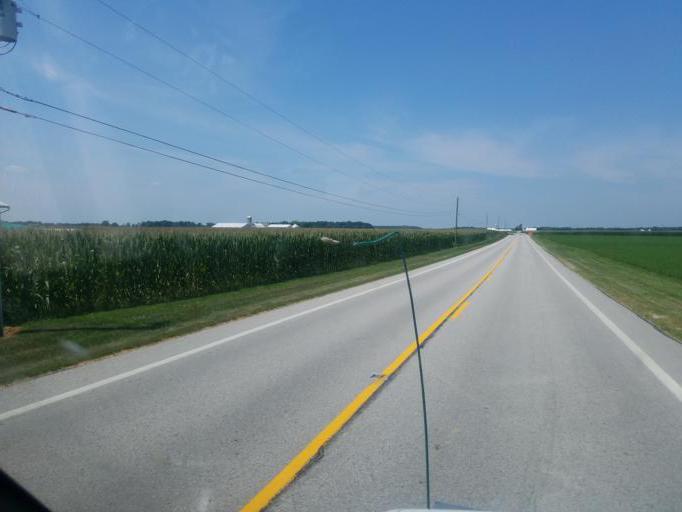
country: US
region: Ohio
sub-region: Auglaize County
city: New Bremen
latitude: 40.4598
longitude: -84.4342
